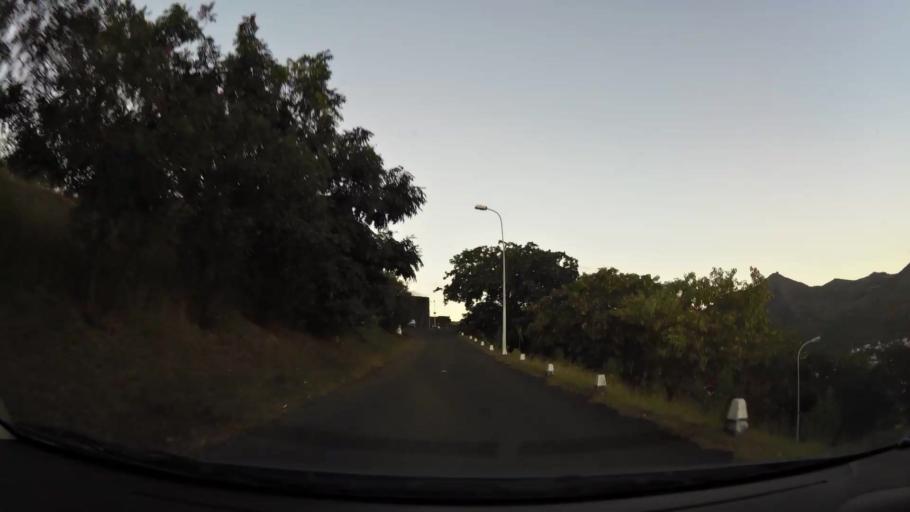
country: MU
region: Port Louis
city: Port Louis
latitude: -20.1633
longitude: 57.5094
